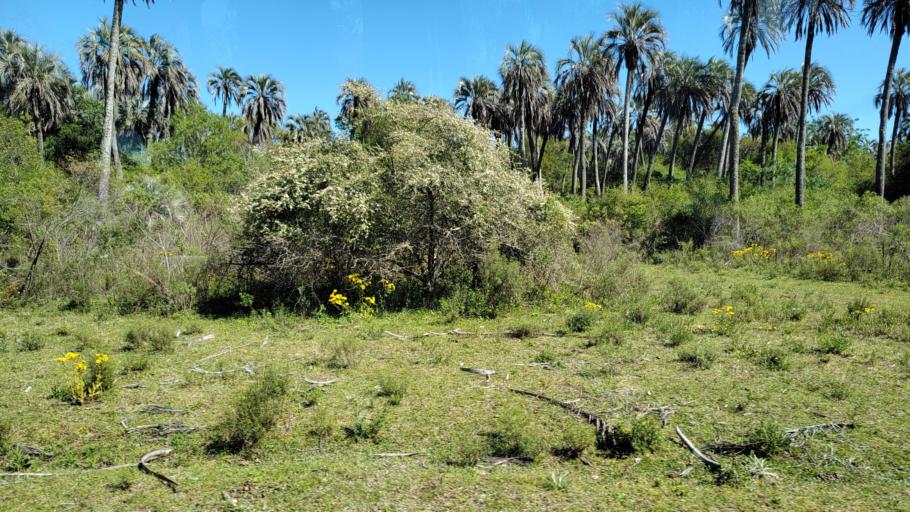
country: AR
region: Entre Rios
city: Ubajay
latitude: -31.8759
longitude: -58.2327
